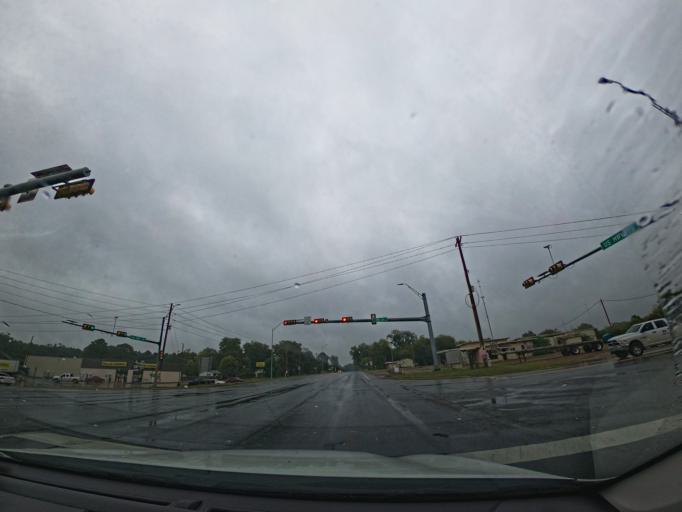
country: US
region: Texas
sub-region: Harrison County
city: Waskom
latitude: 32.3035
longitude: -94.1669
